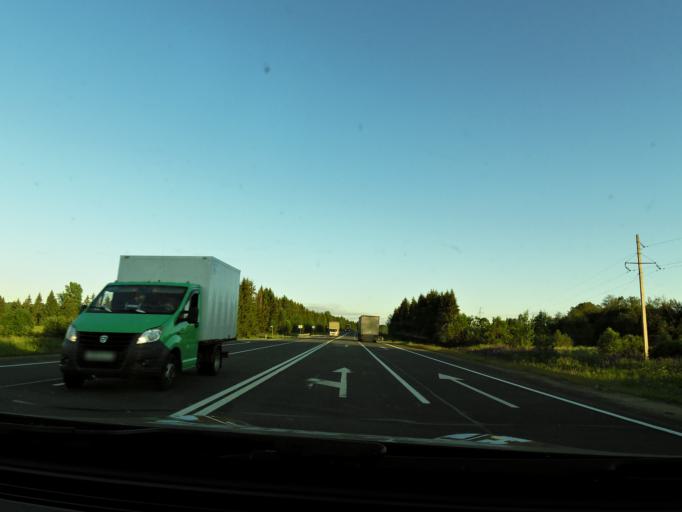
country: RU
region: Vologda
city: Gryazovets
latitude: 58.7275
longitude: 40.2946
